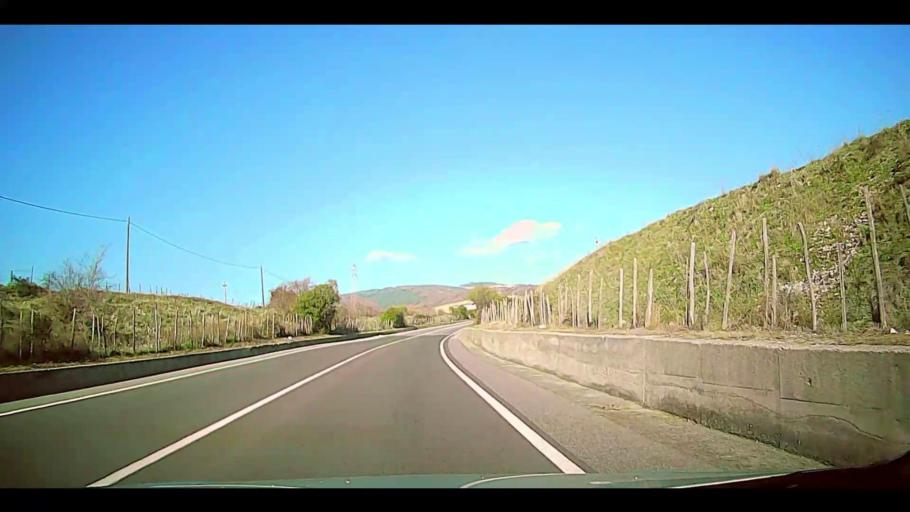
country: IT
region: Calabria
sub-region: Provincia di Crotone
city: Cotronei
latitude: 39.1870
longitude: 16.8181
